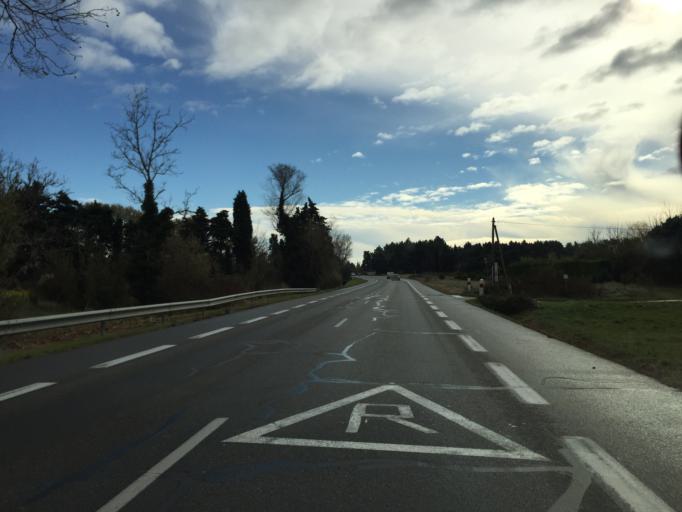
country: FR
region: Provence-Alpes-Cote d'Azur
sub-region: Departement du Vaucluse
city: Velleron
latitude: 43.9750
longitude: 5.0184
